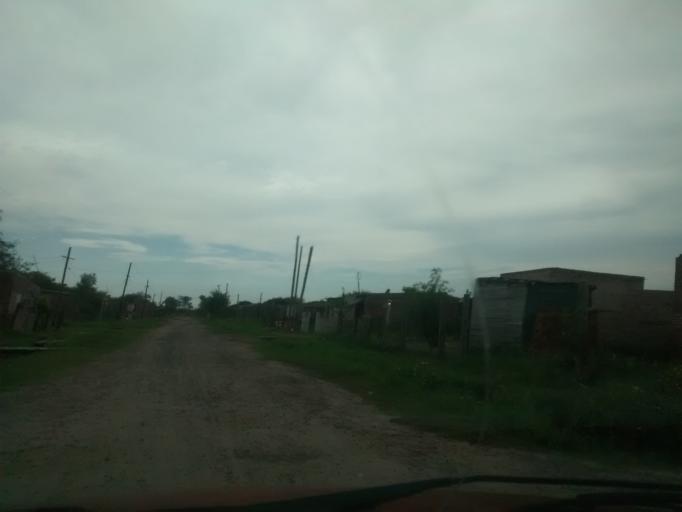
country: AR
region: Chaco
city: Fontana
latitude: -27.4652
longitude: -59.0324
